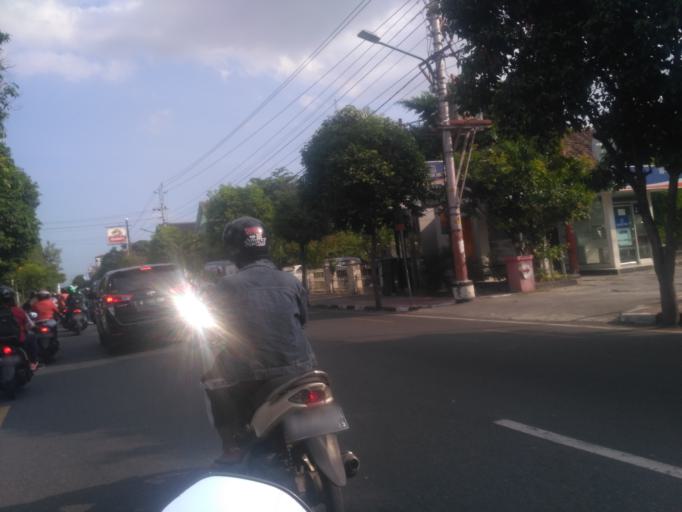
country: ID
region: Daerah Istimewa Yogyakarta
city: Yogyakarta
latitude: -7.7794
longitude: 110.3673
